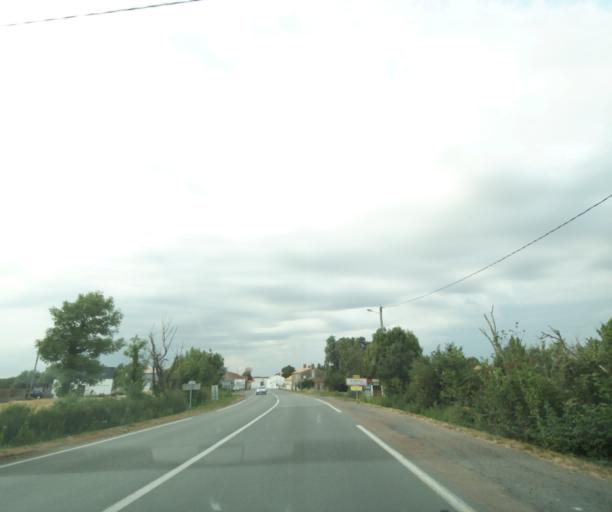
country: FR
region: Pays de la Loire
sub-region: Departement de la Vendee
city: Chaille-les-Marais
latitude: 46.3645
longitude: -0.9888
